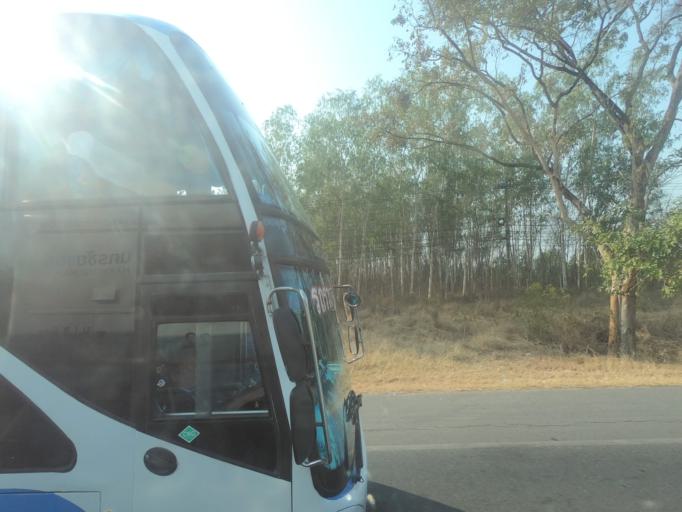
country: TH
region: Khon Kaen
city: Ban Haet
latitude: 16.2612
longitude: 102.7775
